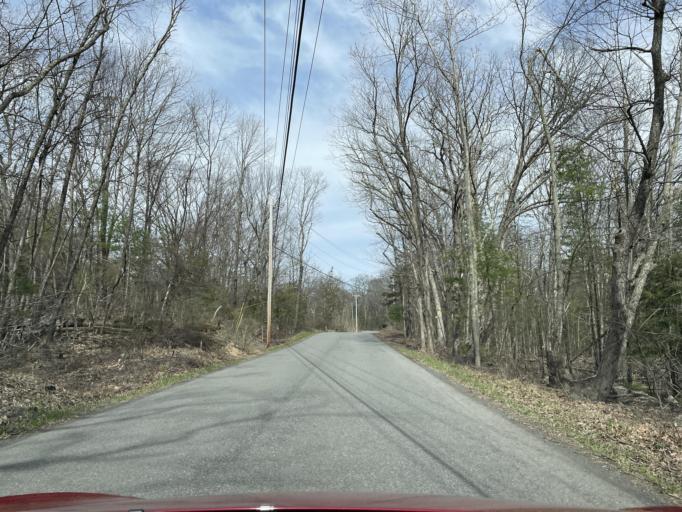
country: US
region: New York
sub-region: Ulster County
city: West Hurley
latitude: 41.9987
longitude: -74.0959
